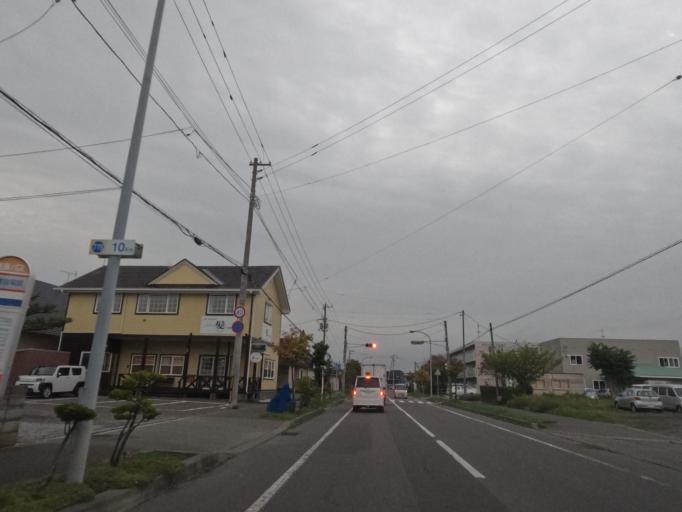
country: JP
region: Hokkaido
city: Date
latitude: 42.4723
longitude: 140.8532
